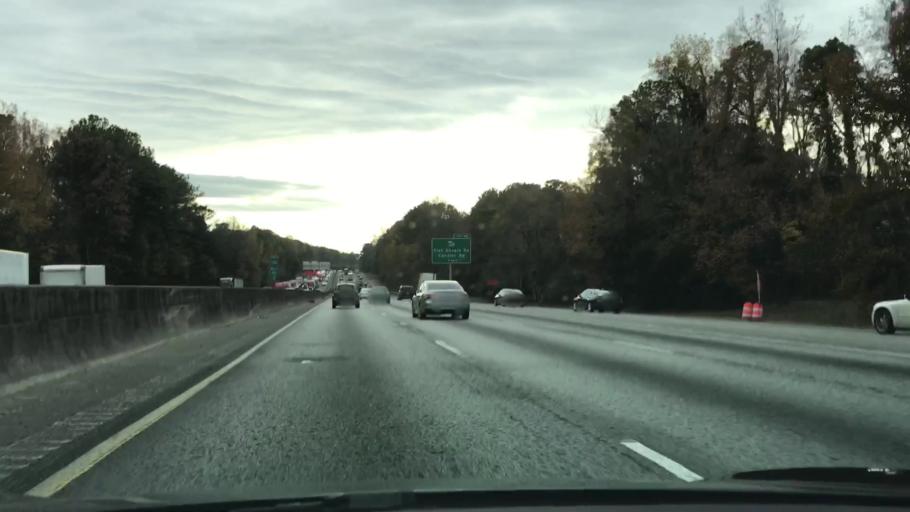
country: US
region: Georgia
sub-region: DeKalb County
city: Panthersville
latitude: 33.7085
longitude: -84.2470
